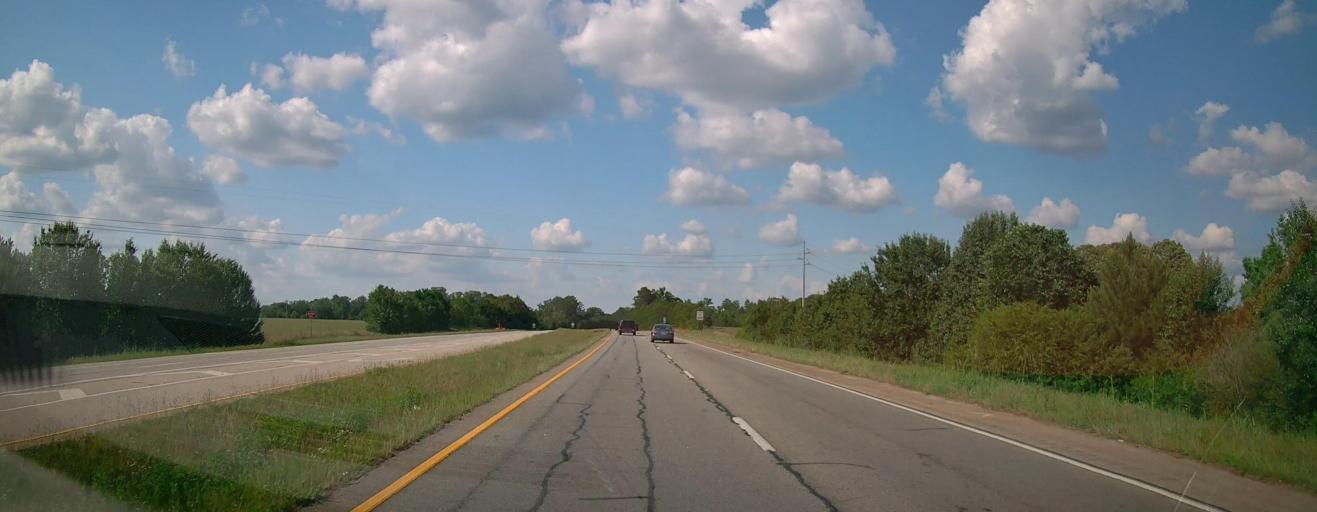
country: US
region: Georgia
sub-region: Henry County
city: Hampton
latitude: 33.3859
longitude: -84.2598
